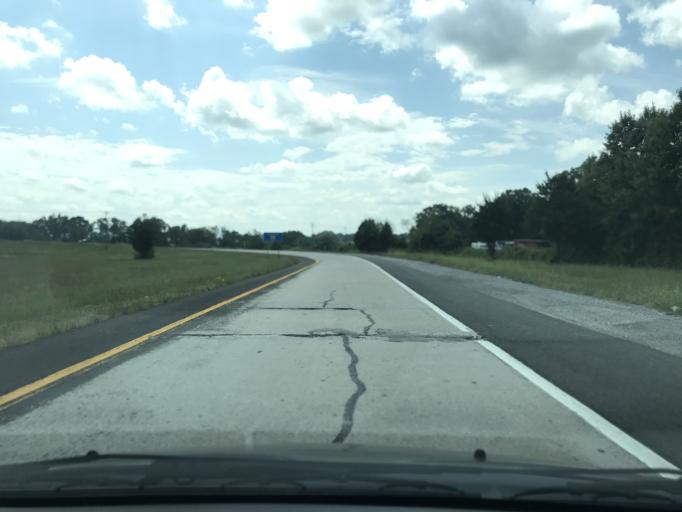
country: US
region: Tennessee
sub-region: Monroe County
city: Sweetwater
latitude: 35.6246
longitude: -84.4915
